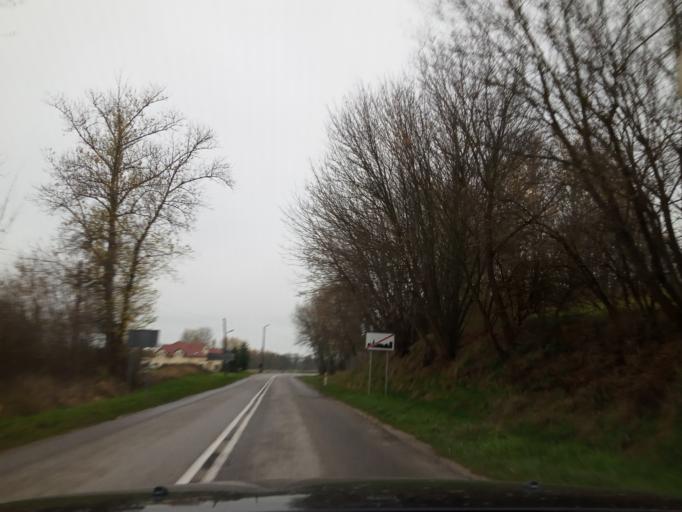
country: PL
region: Swietokrzyskie
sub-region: Powiat pinczowski
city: Dzialoszyce
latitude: 50.3675
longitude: 20.3463
